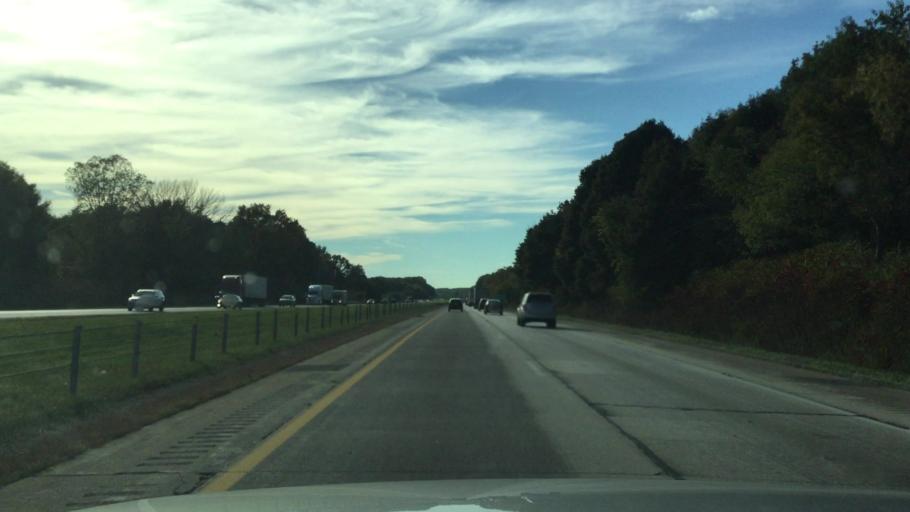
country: US
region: Michigan
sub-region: Calhoun County
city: Brownlee Park
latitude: 42.2866
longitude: -85.1261
